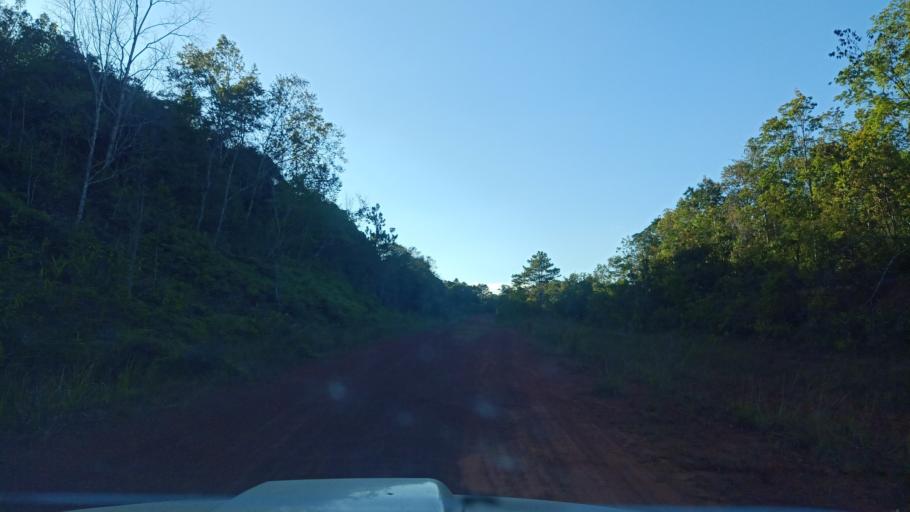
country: LA
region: Attapu
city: Attapu
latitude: 15.0316
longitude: 106.6992
